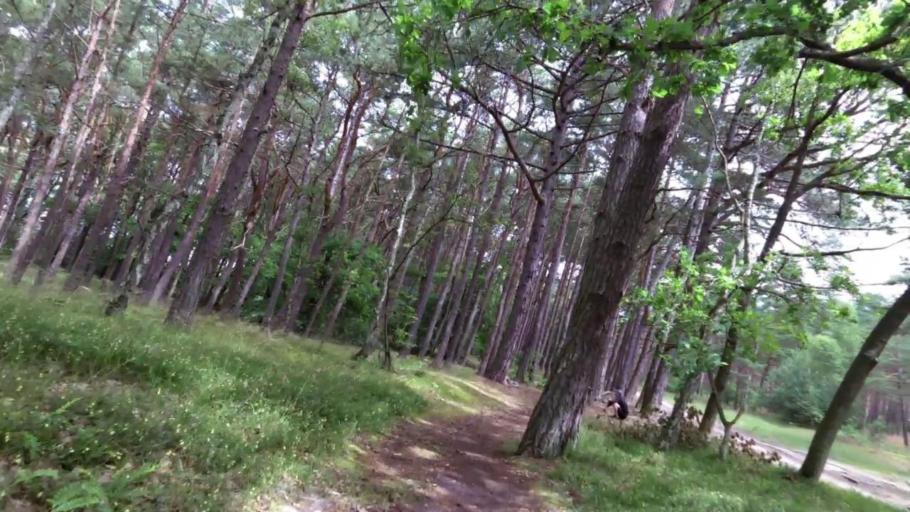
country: PL
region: West Pomeranian Voivodeship
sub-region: Powiat slawienski
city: Darlowo
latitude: 54.5014
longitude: 16.4566
